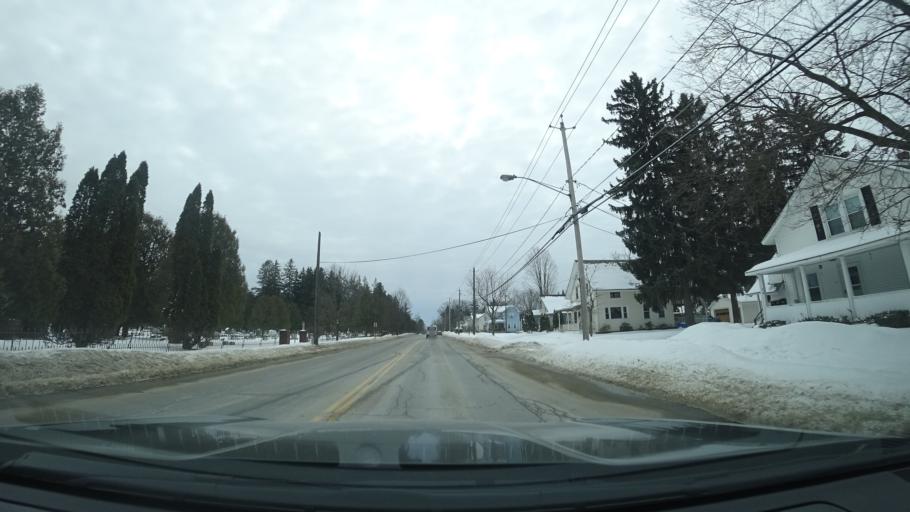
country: US
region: New York
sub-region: Saratoga County
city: South Glens Falls
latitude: 43.2932
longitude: -73.6295
